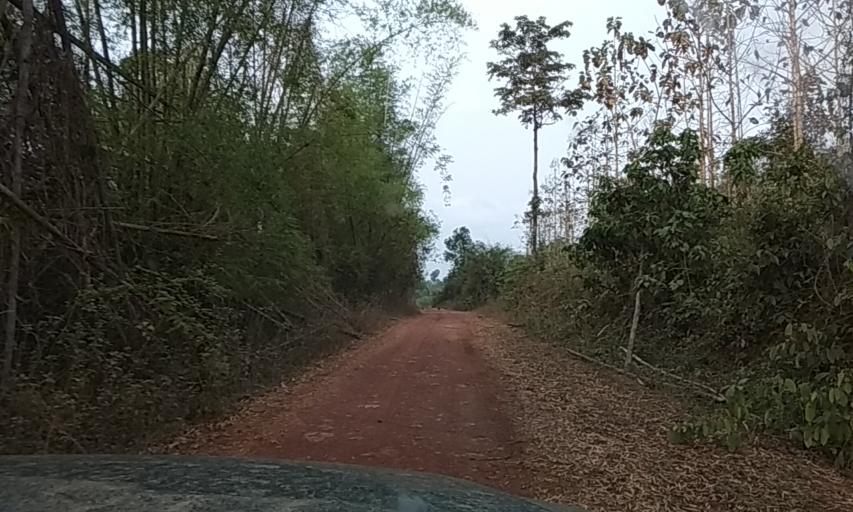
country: TH
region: Nan
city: Mae Charim
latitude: 18.4277
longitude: 101.1746
